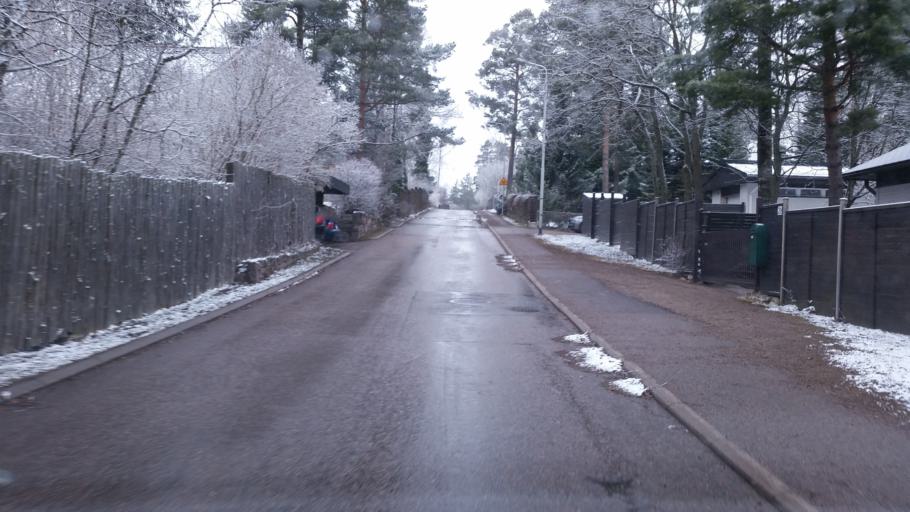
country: FI
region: Uusimaa
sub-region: Helsinki
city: Koukkuniemi
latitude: 60.1643
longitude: 24.7934
